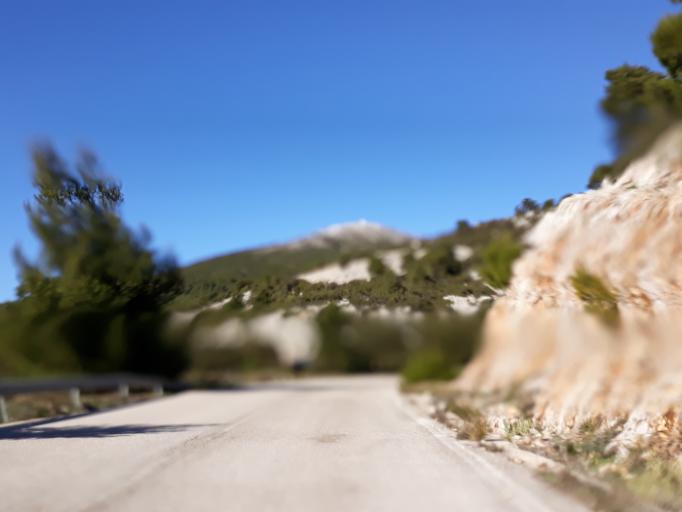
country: GR
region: Attica
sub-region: Nomarchia Dytikis Attikis
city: Fyli
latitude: 38.1394
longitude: 23.6479
